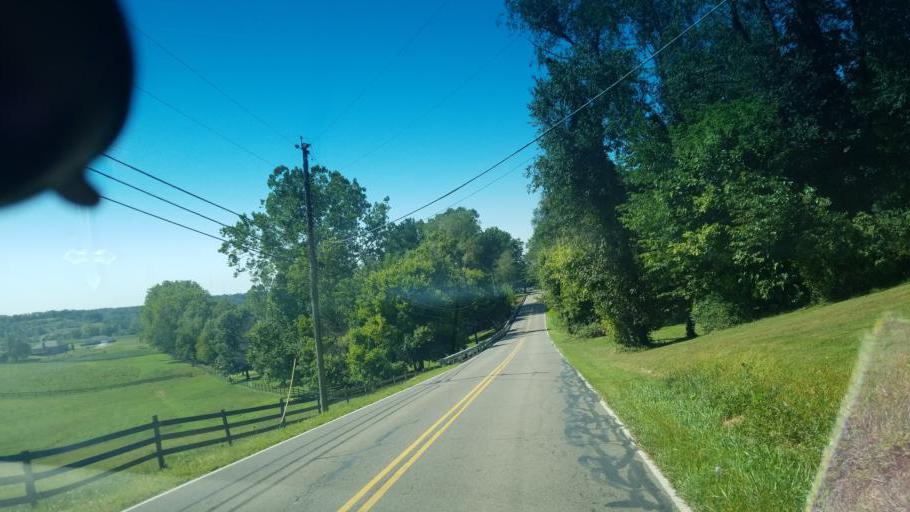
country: US
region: Ohio
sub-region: Licking County
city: Newark
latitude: 40.1157
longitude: -82.4007
